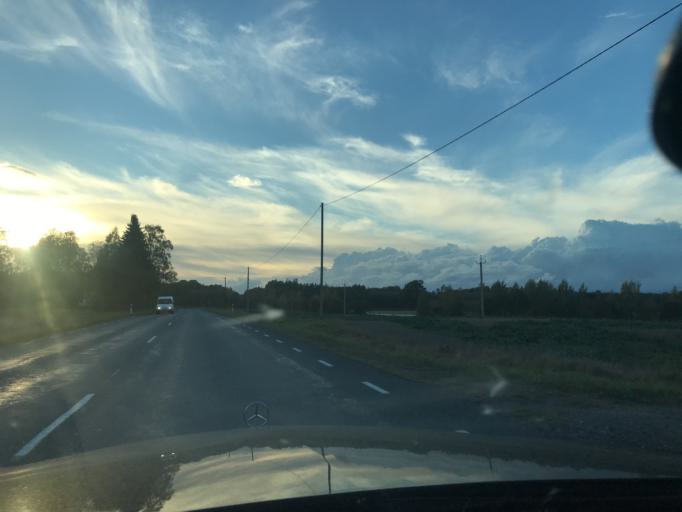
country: EE
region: Vorumaa
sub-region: Antsla vald
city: Vana-Antsla
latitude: 57.8798
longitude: 26.7050
